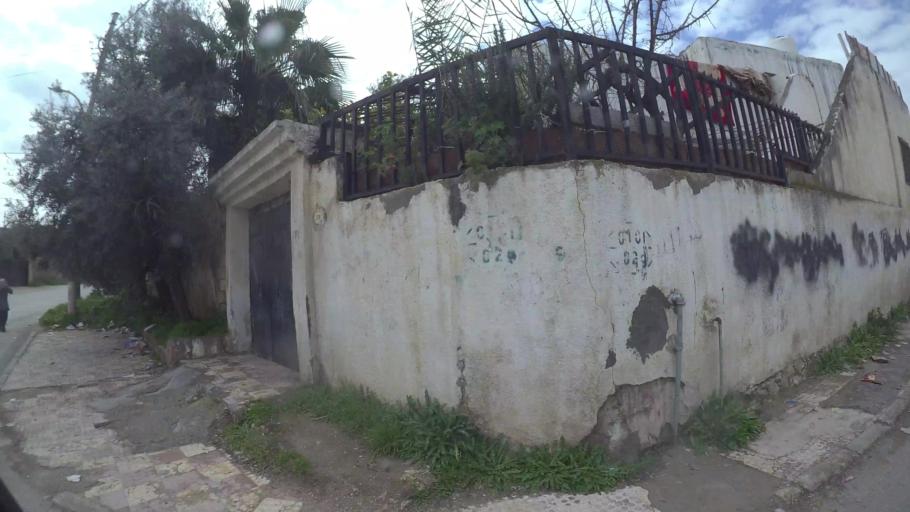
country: JO
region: Amman
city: Al Jubayhah
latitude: 32.0599
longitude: 35.8322
